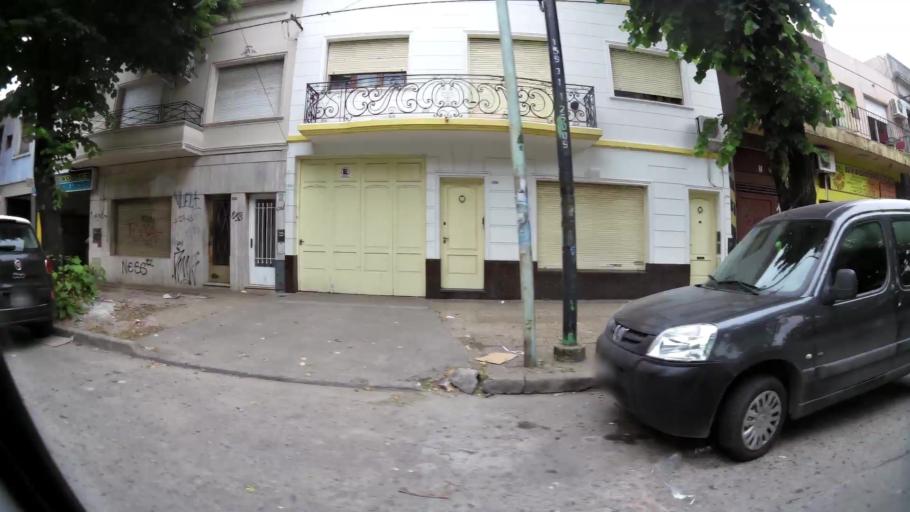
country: AR
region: Buenos Aires
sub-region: Partido de La Plata
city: La Plata
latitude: -34.9336
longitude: -57.9556
